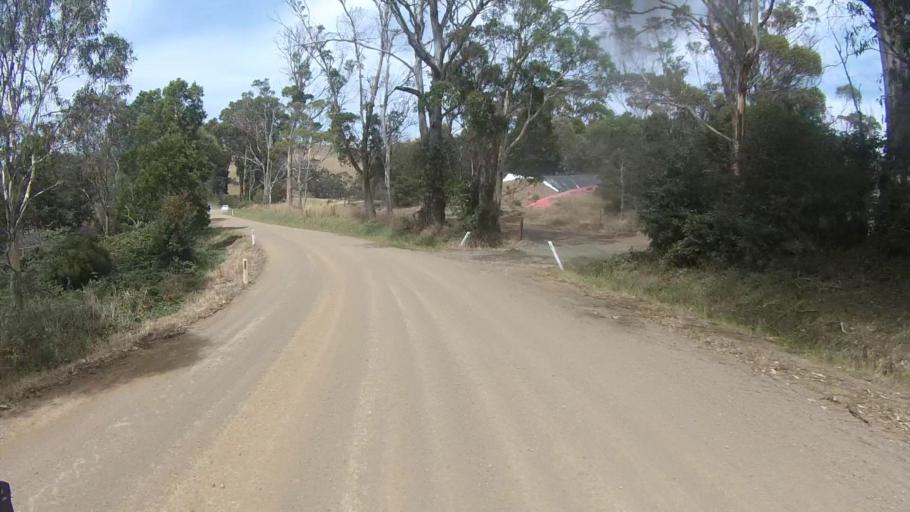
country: AU
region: Tasmania
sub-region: Sorell
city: Sorell
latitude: -42.8184
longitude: 147.8239
